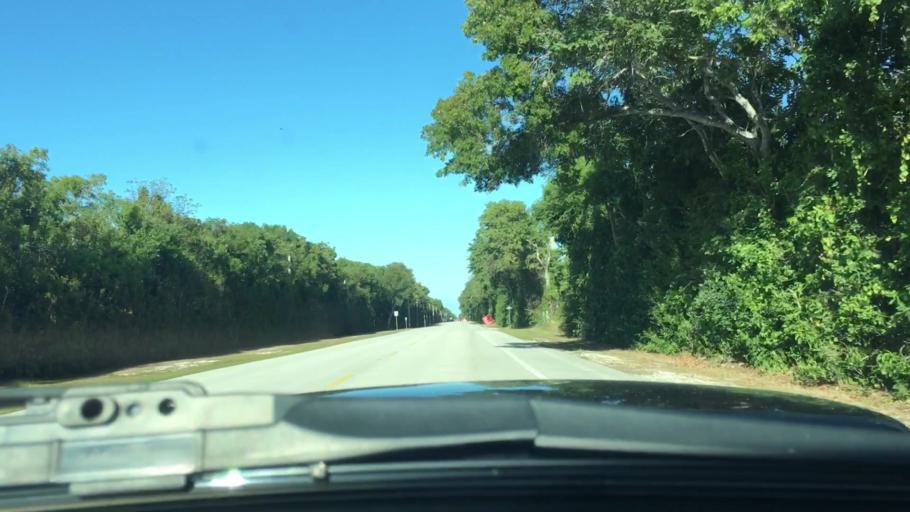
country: US
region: Florida
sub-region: Monroe County
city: North Key Largo
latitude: 25.1804
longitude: -80.3660
